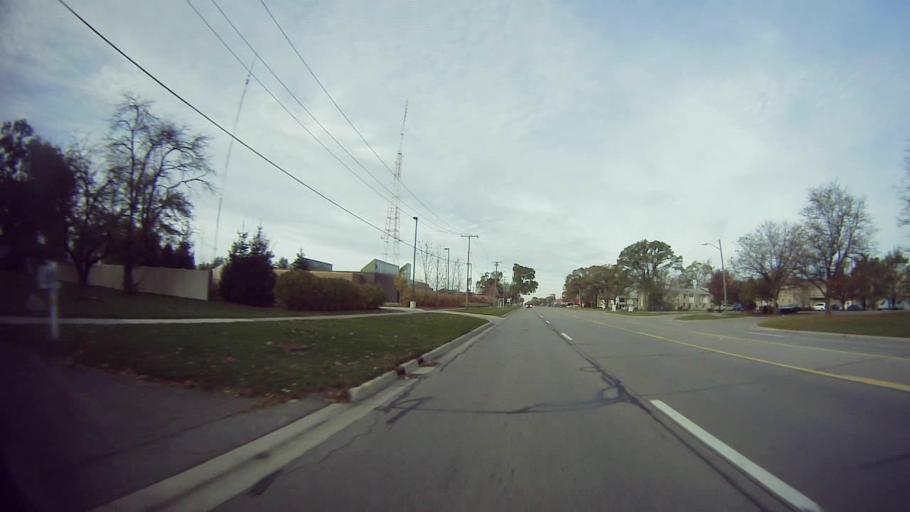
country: US
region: Michigan
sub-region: Oakland County
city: Oak Park
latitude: 42.4739
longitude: -83.1980
